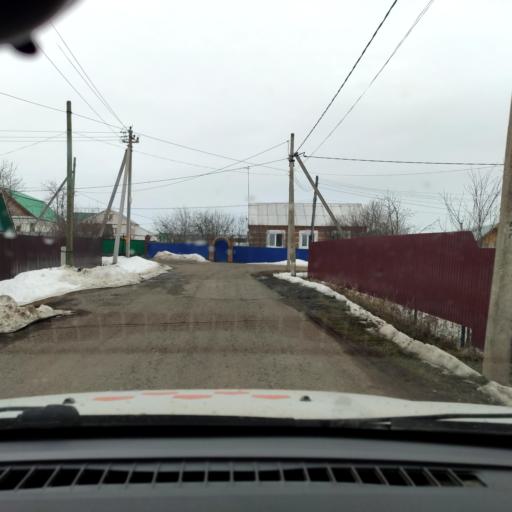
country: RU
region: Bashkortostan
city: Kushnarenkovo
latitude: 55.1084
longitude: 55.3325
